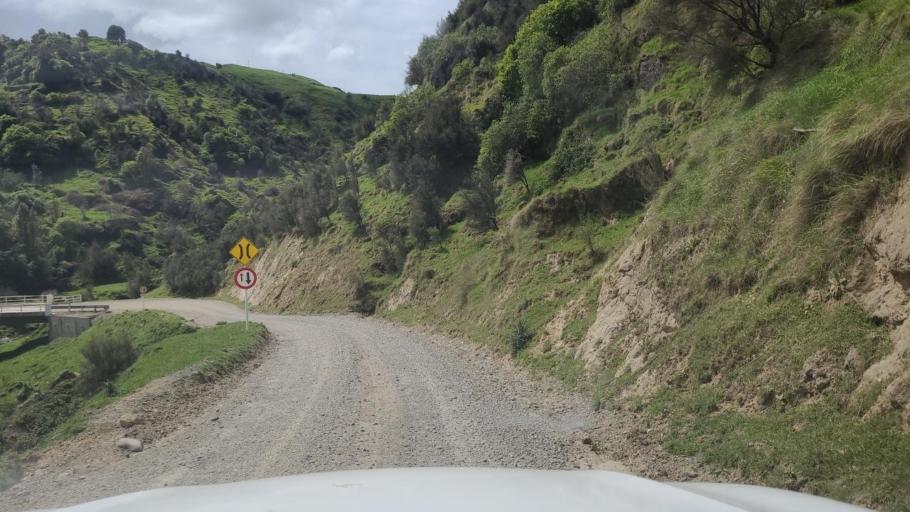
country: NZ
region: Hawke's Bay
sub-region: Napier City
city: Taradale
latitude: -39.2679
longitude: 176.6637
